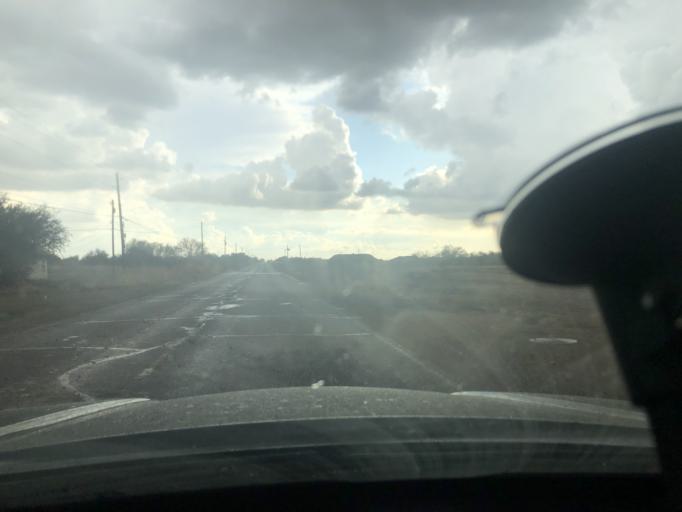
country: US
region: Arizona
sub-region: Maricopa County
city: Scottsdale
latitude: 33.4921
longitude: -111.8827
